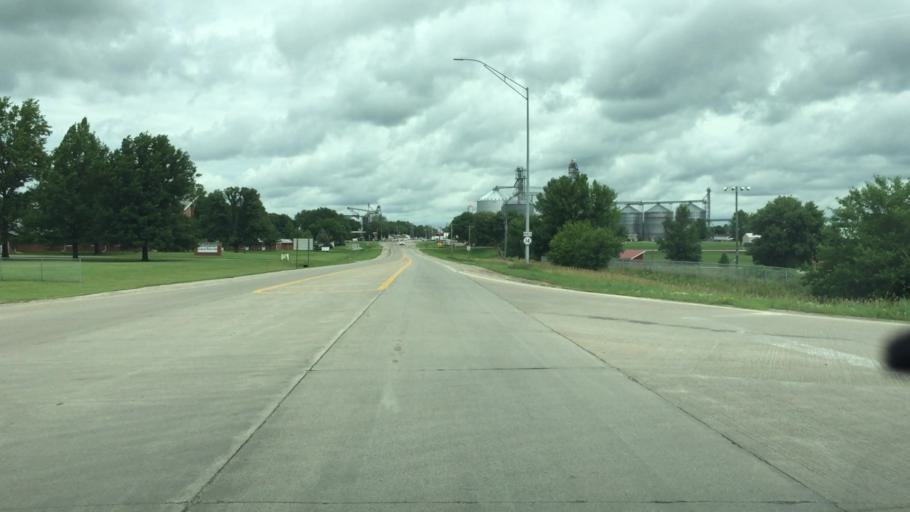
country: US
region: Iowa
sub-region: Jasper County
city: Monroe
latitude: 41.5125
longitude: -93.1012
